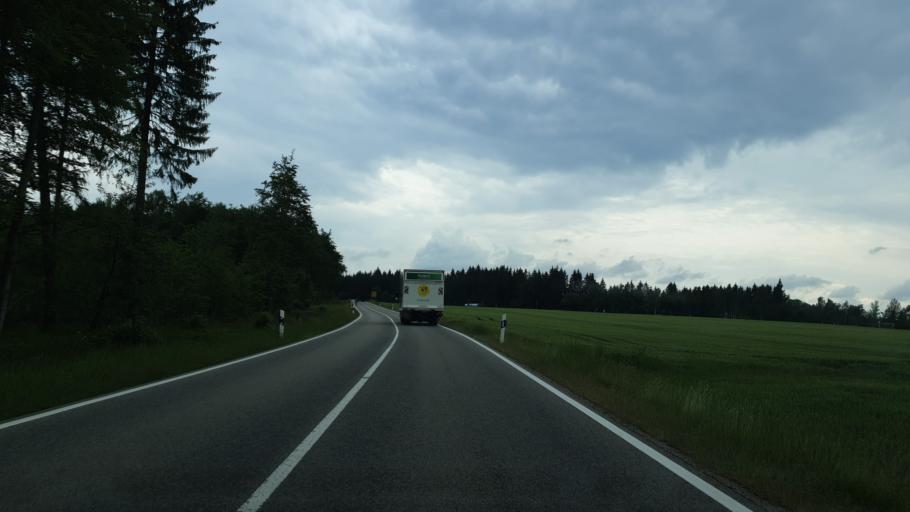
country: DE
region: Saxony
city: Hammerbrucke
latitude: 50.4746
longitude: 12.4322
